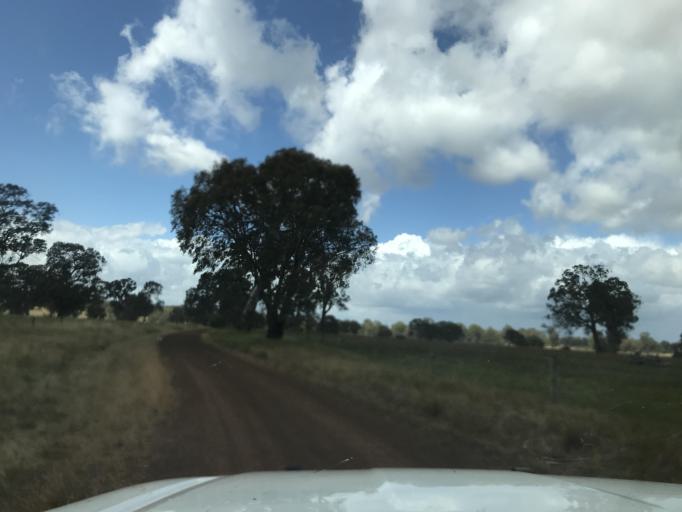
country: AU
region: South Australia
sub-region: Wattle Range
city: Penola
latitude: -37.1904
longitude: 141.4315
